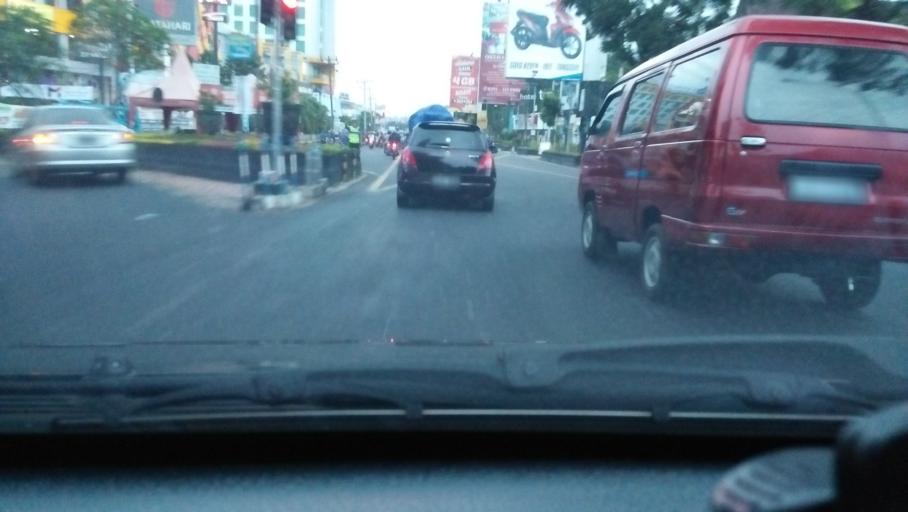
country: ID
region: Central Java
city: Mertoyudan
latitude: -7.5025
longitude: 110.2237
